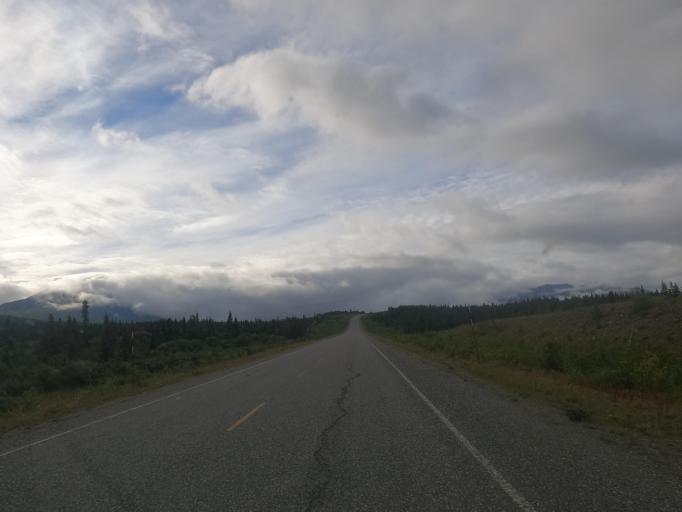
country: CA
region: Yukon
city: Haines Junction
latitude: 59.9511
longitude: -136.8063
